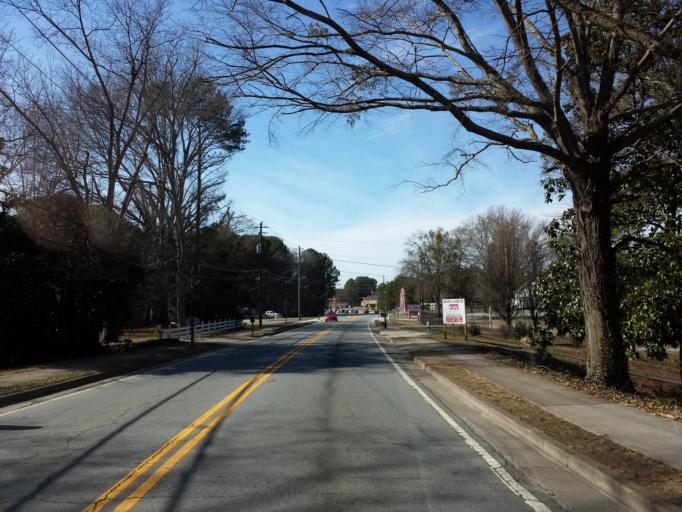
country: US
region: Georgia
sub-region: Cobb County
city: Kennesaw
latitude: 34.0274
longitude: -84.6240
